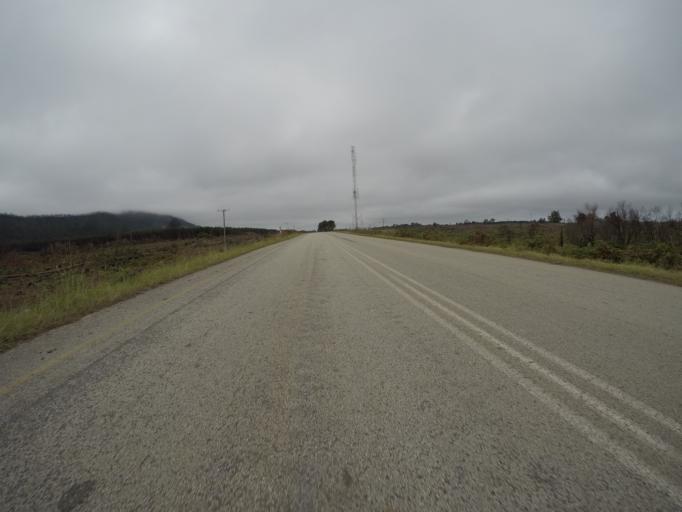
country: ZA
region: Eastern Cape
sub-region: Cacadu District Municipality
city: Kareedouw
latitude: -33.9821
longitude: 24.0528
